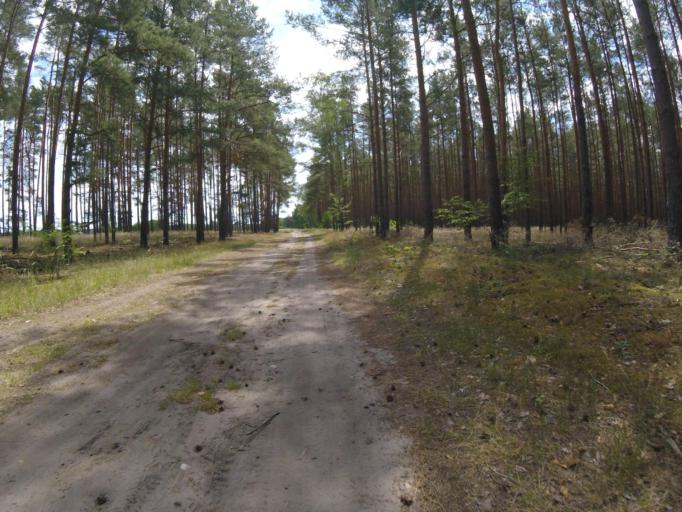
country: DE
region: Brandenburg
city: Gross Koris
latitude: 52.1328
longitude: 13.6688
